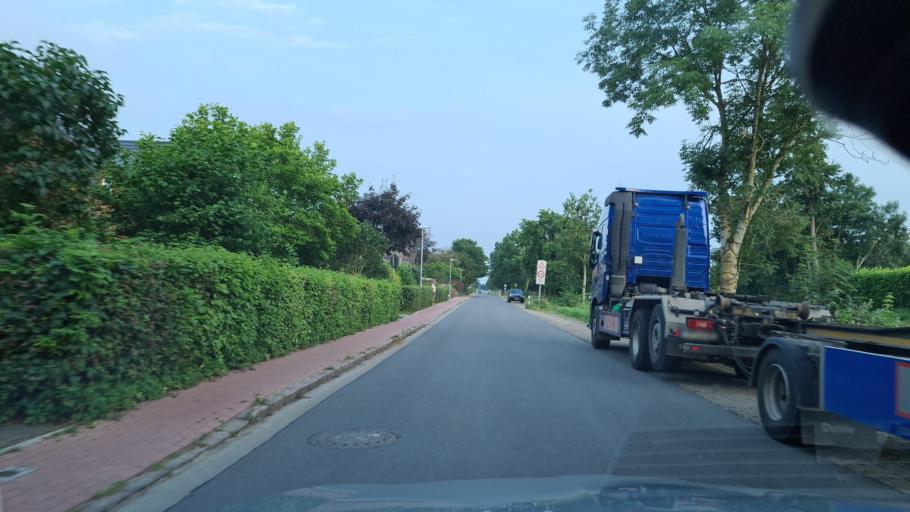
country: DE
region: Schleswig-Holstein
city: Oldenswort
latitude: 54.3717
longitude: 8.9433
